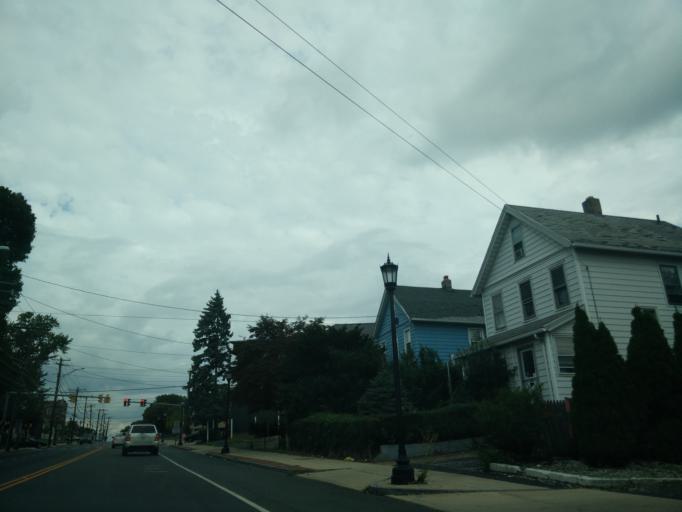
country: US
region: Connecticut
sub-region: Fairfield County
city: Stratford
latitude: 41.1927
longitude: -73.1474
